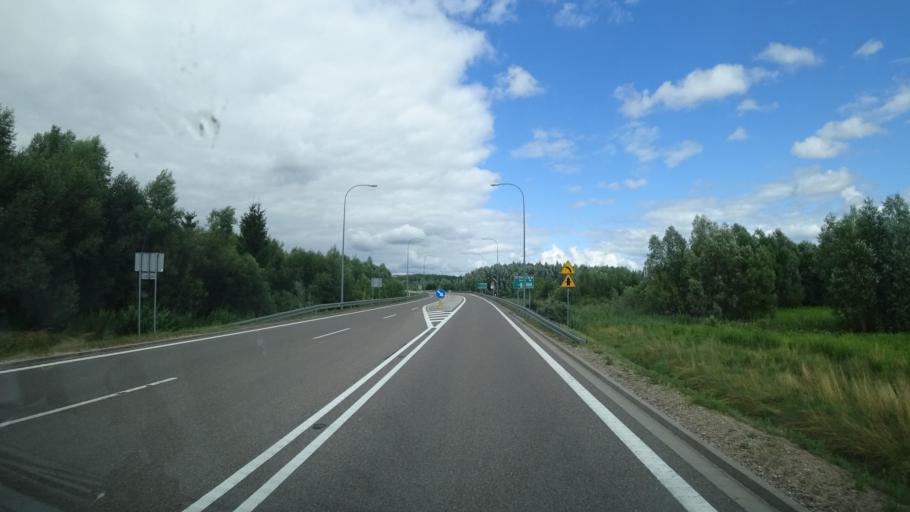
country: PL
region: Warmian-Masurian Voivodeship
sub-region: Powiat goldapski
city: Goldap
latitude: 54.3174
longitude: 22.2919
